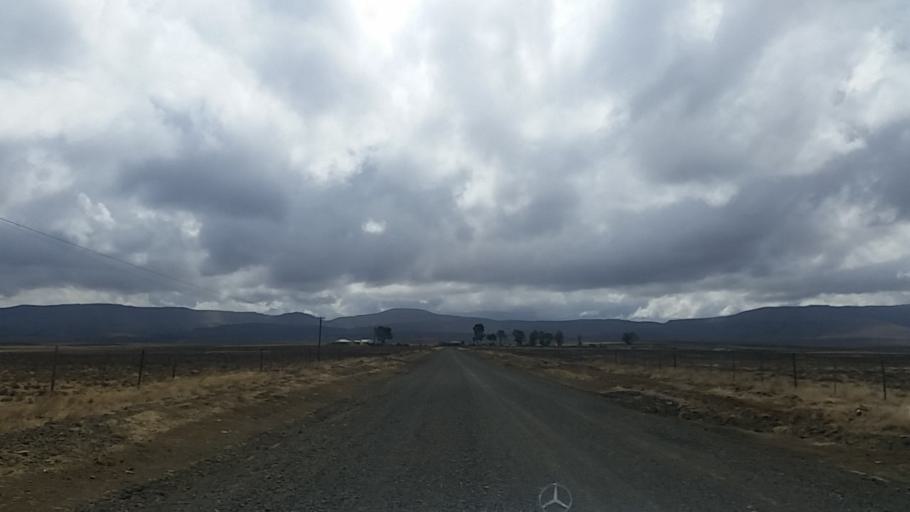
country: ZA
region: Eastern Cape
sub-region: Cacadu District Municipality
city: Graaff-Reinet
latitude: -31.9101
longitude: 24.7640
